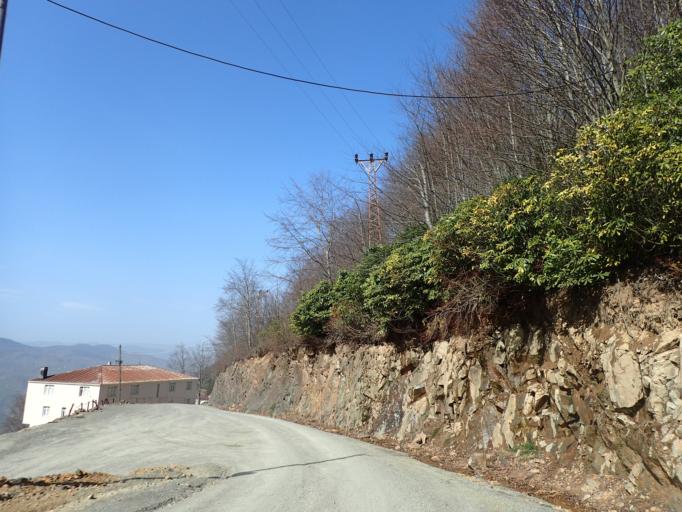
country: TR
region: Ordu
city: Kabaduz
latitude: 40.8135
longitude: 37.8884
